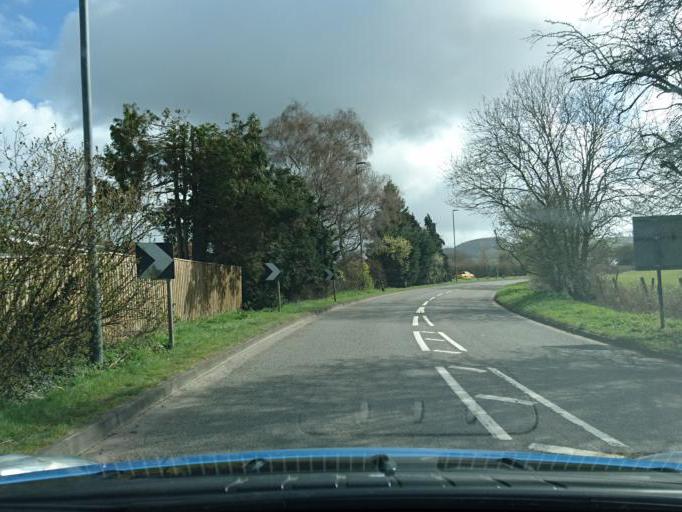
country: GB
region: England
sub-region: South Gloucestershire
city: Pucklechurch
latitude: 51.4526
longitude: -2.4173
